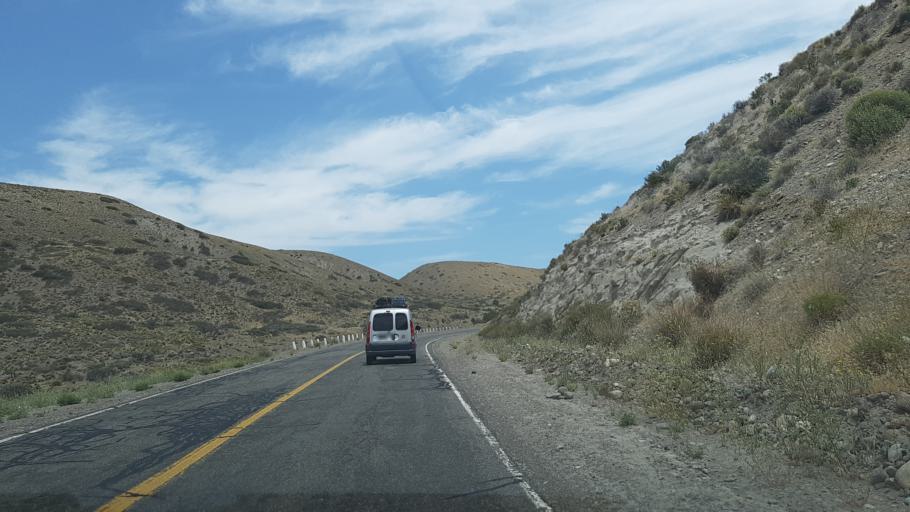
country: AR
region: Rio Negro
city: Pilcaniyeu
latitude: -40.4734
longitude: -70.6601
